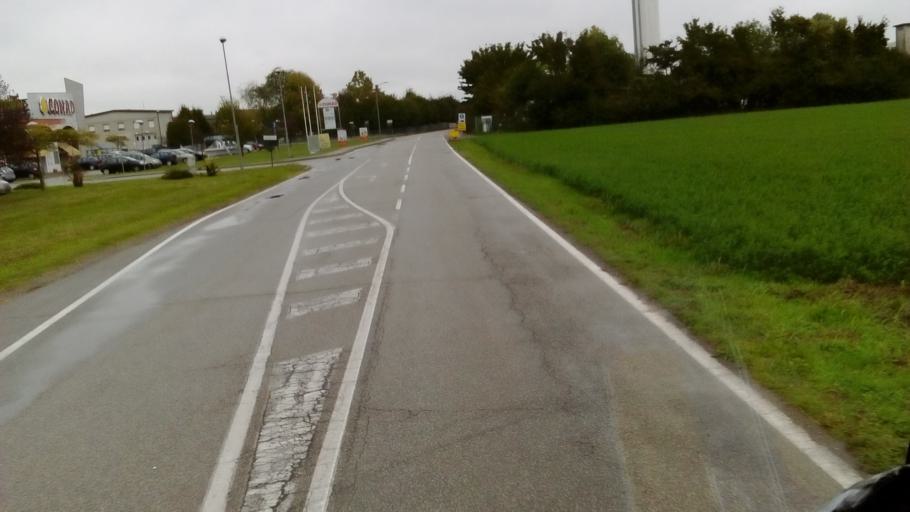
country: IT
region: Emilia-Romagna
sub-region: Provincia di Reggio Emilia
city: Luzzara
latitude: 44.9538
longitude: 10.6891
